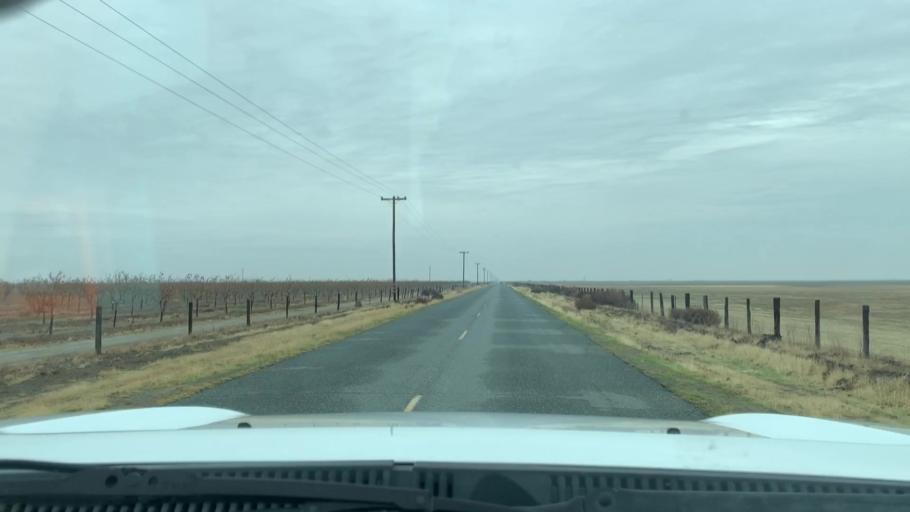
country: US
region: California
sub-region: Tulare County
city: Alpaugh
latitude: 35.7608
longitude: -119.5579
